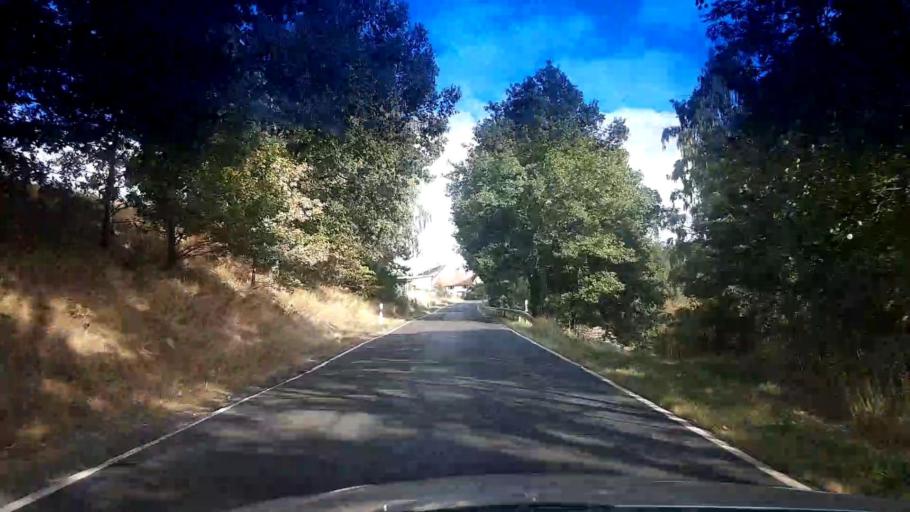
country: DE
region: Bavaria
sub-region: Upper Palatinate
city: Neualbenreuth
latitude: 49.9873
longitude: 12.4137
